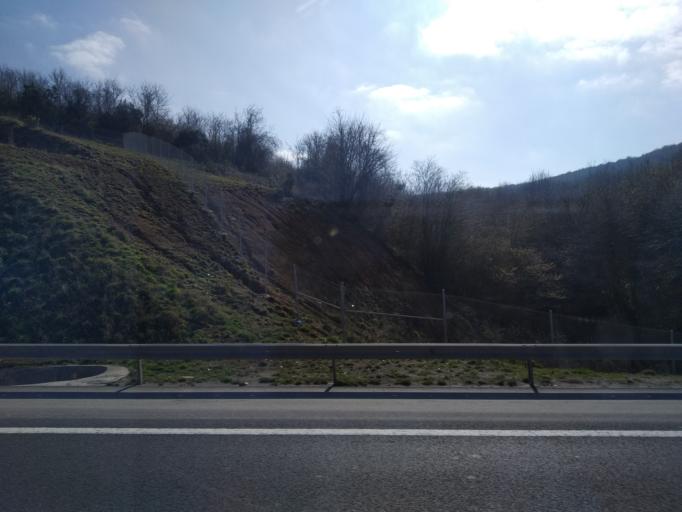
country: TR
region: Istanbul
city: Arikoey
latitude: 41.2207
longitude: 29.0038
